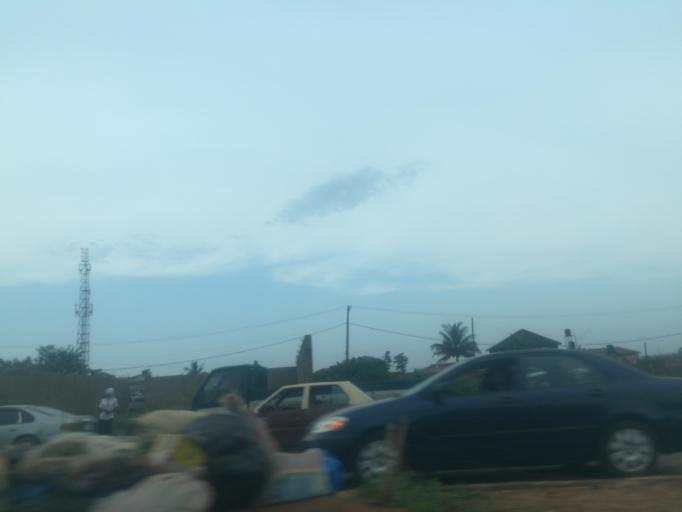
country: NG
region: Oyo
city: Ibadan
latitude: 7.3657
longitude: 3.8156
